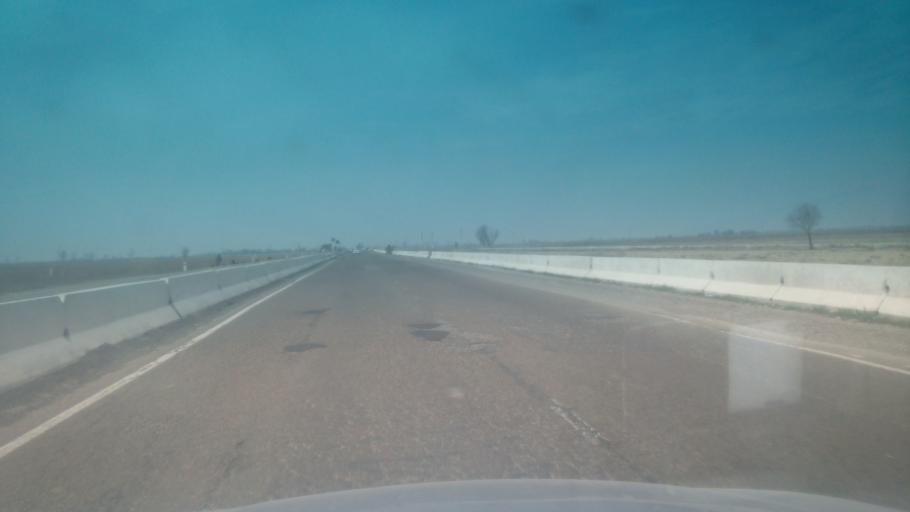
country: KZ
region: Ongtustik Qazaqstan
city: Myrzakent
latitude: 40.5183
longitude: 68.4733
